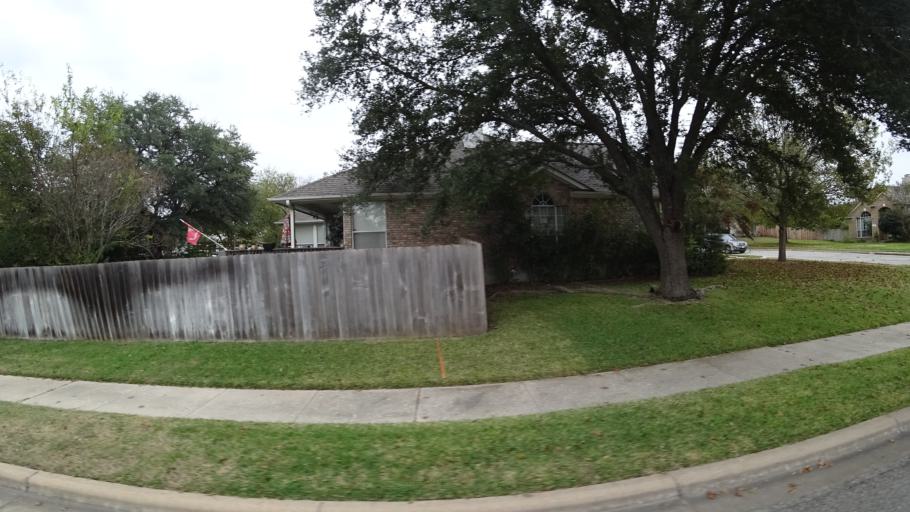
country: US
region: Texas
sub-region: Travis County
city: Pflugerville
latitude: 30.4449
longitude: -97.6259
